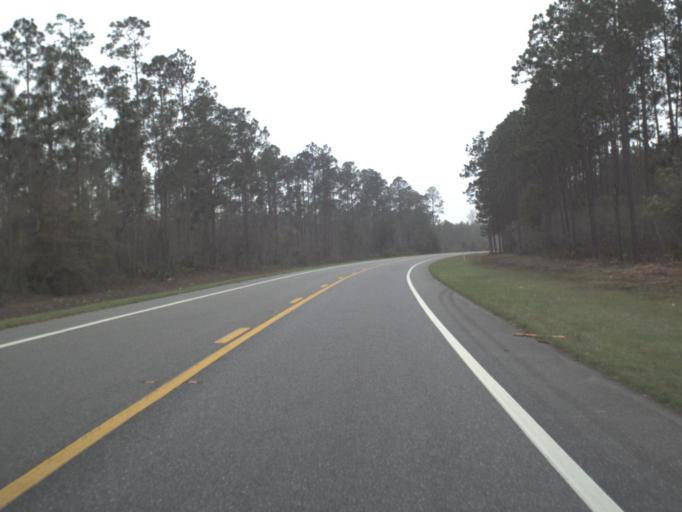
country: US
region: Florida
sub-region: Gadsden County
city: Gretna
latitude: 30.4500
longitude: -84.7561
